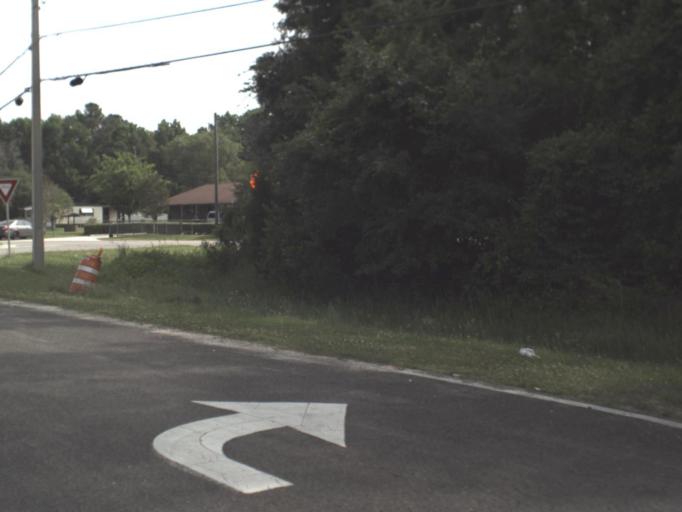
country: US
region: Florida
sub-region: Clay County
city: Green Cove Springs
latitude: 30.0329
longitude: -81.7088
